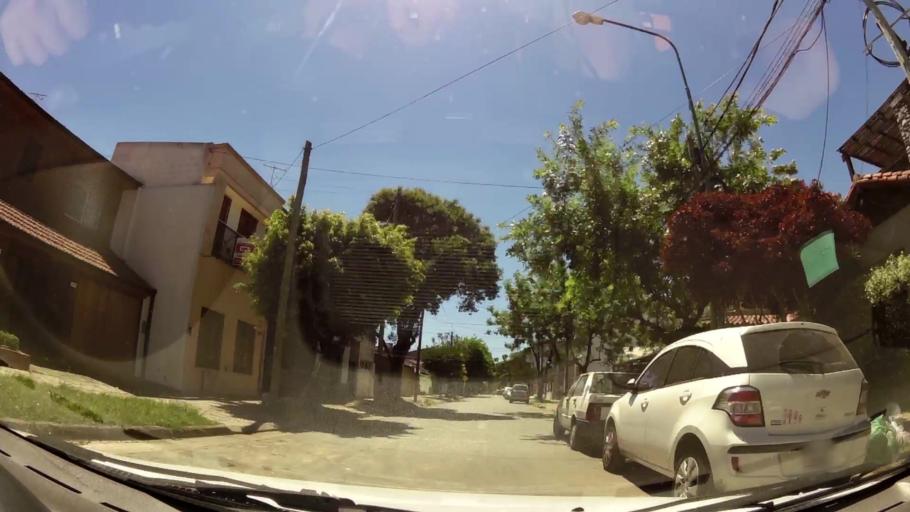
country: AR
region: Buenos Aires
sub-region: Partido de Vicente Lopez
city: Olivos
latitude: -34.5052
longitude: -58.5051
